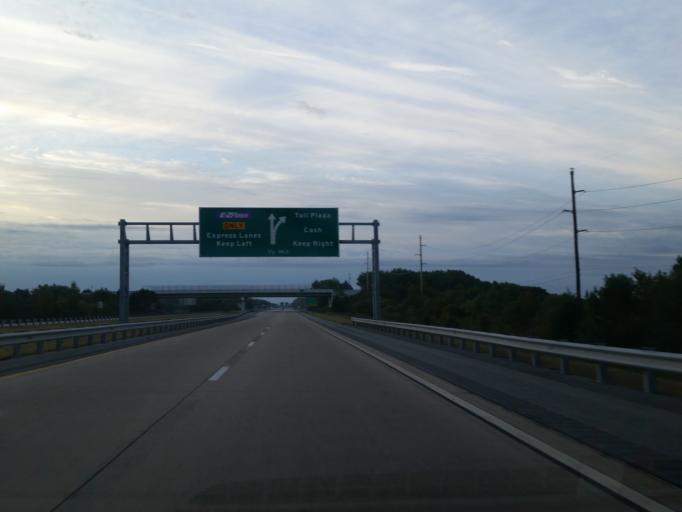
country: US
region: Delaware
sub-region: Kent County
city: Dover
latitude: 39.1935
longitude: -75.5277
